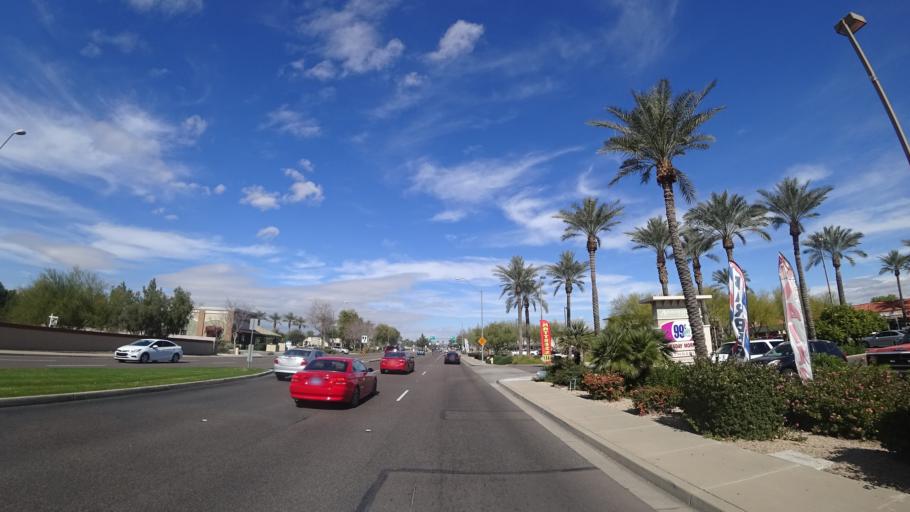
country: US
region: Arizona
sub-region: Maricopa County
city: Peoria
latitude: 33.6652
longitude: -112.2029
